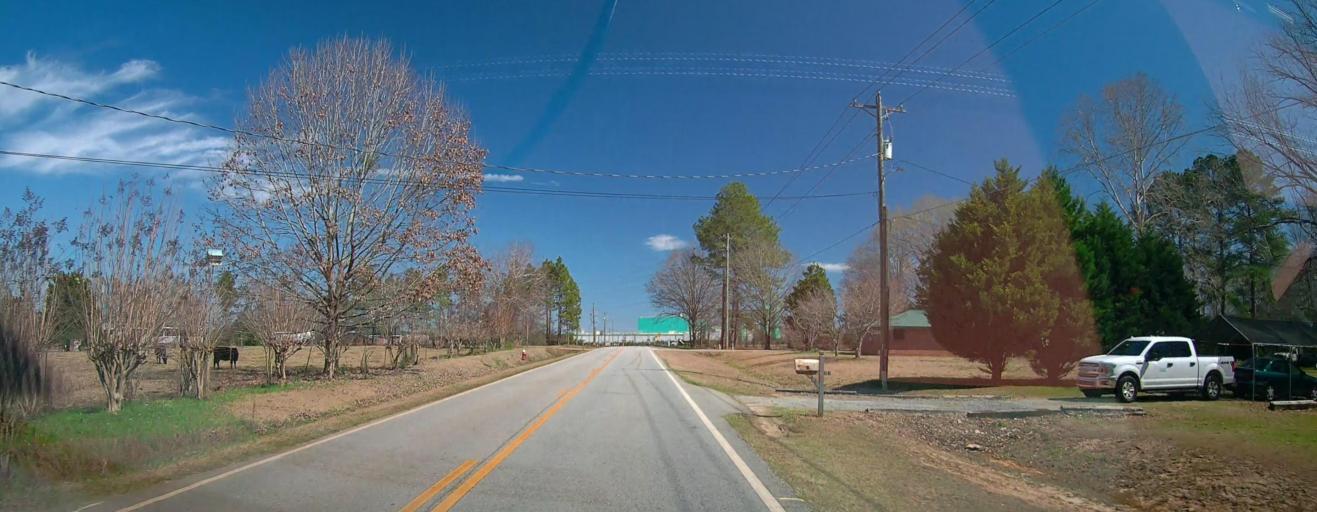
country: US
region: Georgia
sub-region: Houston County
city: Perry
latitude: 32.4854
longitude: -83.6165
